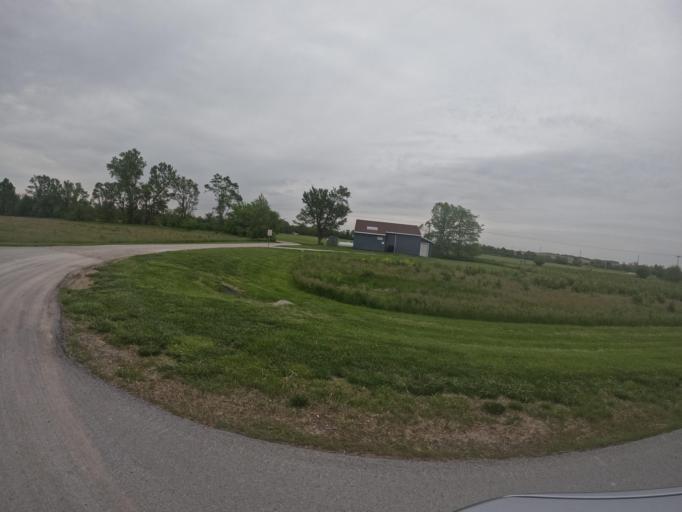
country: US
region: Nebraska
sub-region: Sarpy County
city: Offutt Air Force Base
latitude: 41.0485
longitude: -95.9527
